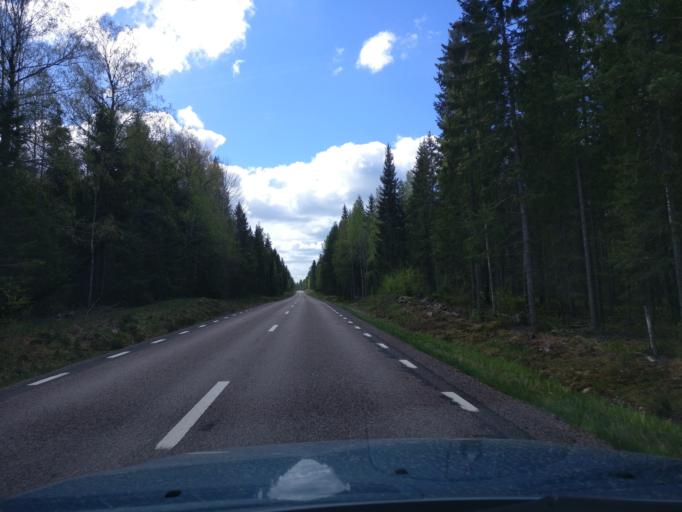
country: SE
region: Vaermland
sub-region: Karlstads Kommun
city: Molkom
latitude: 59.7508
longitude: 13.6865
